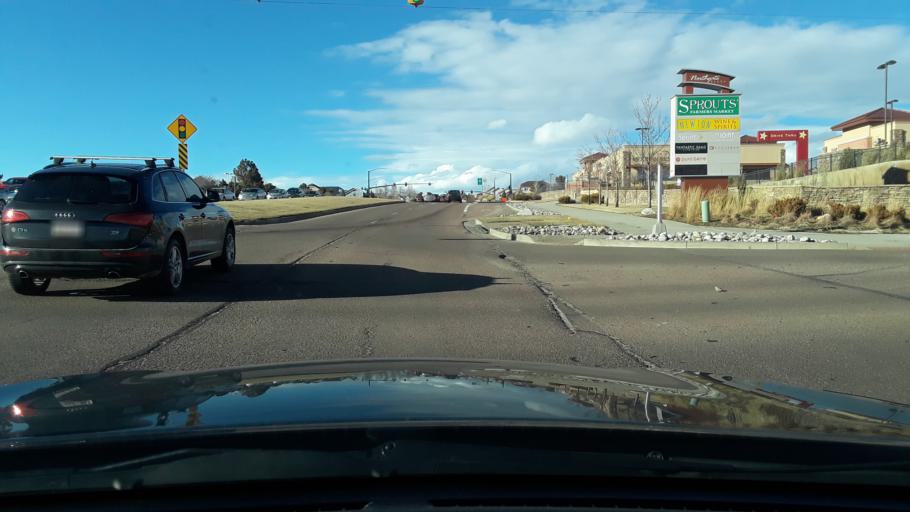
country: US
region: Colorado
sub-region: El Paso County
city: Gleneagle
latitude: 39.0249
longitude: -104.8170
